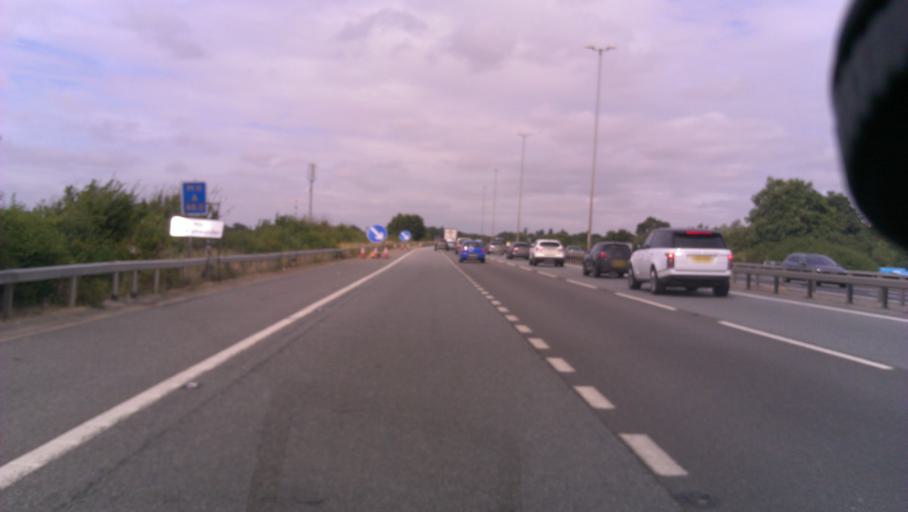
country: GB
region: England
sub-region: Essex
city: Stansted
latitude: 51.8823
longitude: 0.2048
